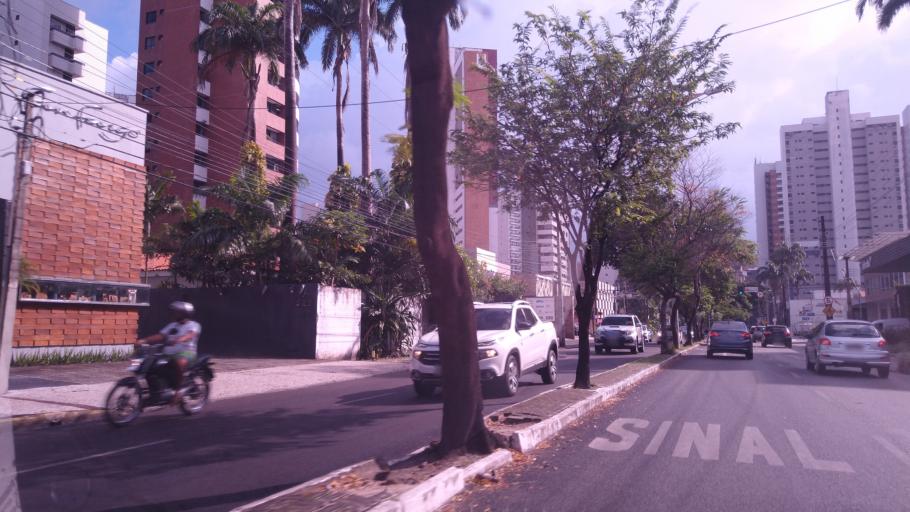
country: BR
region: Ceara
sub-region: Fortaleza
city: Fortaleza
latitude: -3.7326
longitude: -38.4918
